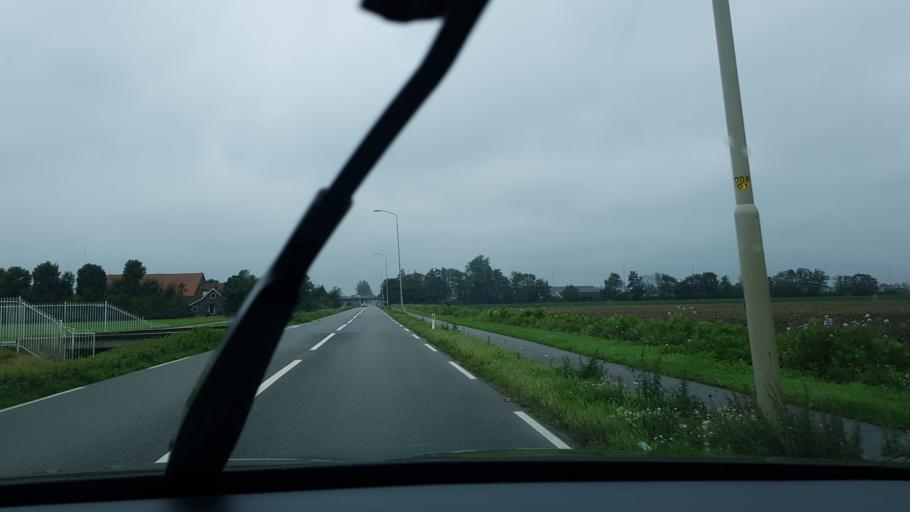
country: NL
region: North Holland
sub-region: Gemeente Haarlemmermeer
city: Hoofddorp
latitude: 52.3640
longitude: 4.7367
